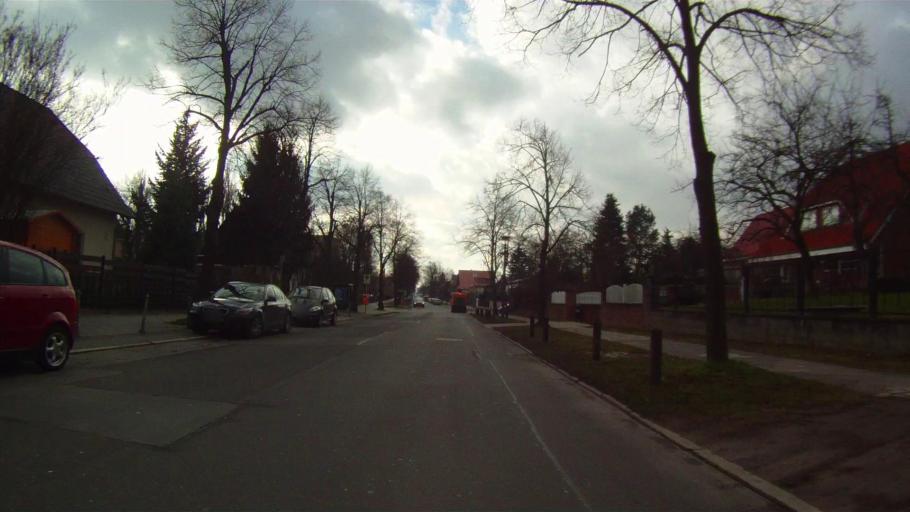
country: DE
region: Berlin
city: Marzahn
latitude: 52.5304
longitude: 13.5583
